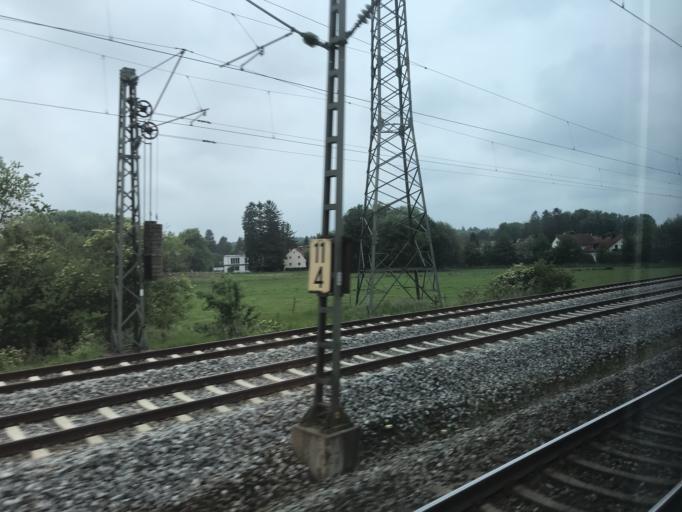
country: DE
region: Bavaria
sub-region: Upper Bavaria
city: Pasing
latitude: 48.1706
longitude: 11.4190
